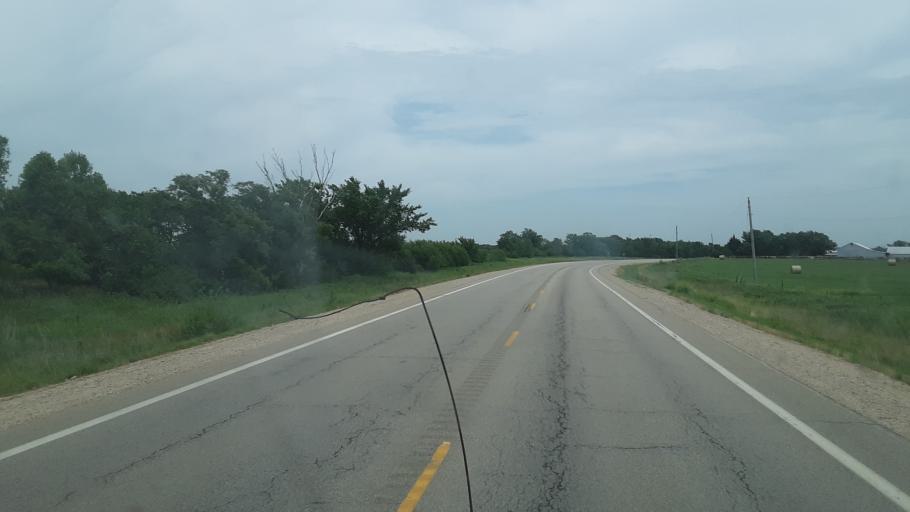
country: US
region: Kansas
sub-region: Woodson County
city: Yates Center
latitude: 37.8784
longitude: -95.7713
